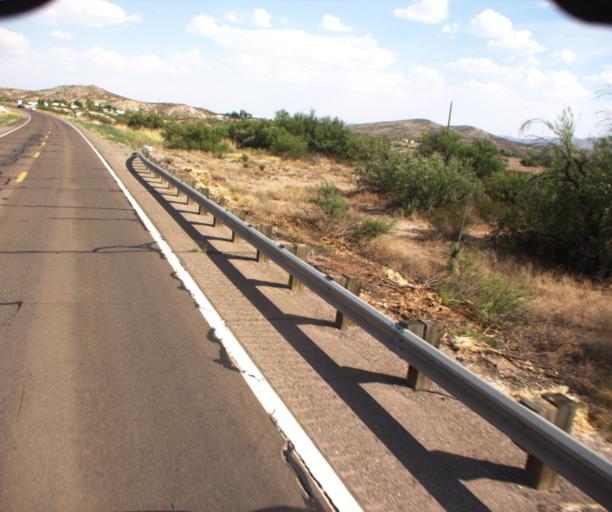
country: US
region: Arizona
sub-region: Greenlee County
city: Clifton
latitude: 32.7700
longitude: -109.1517
